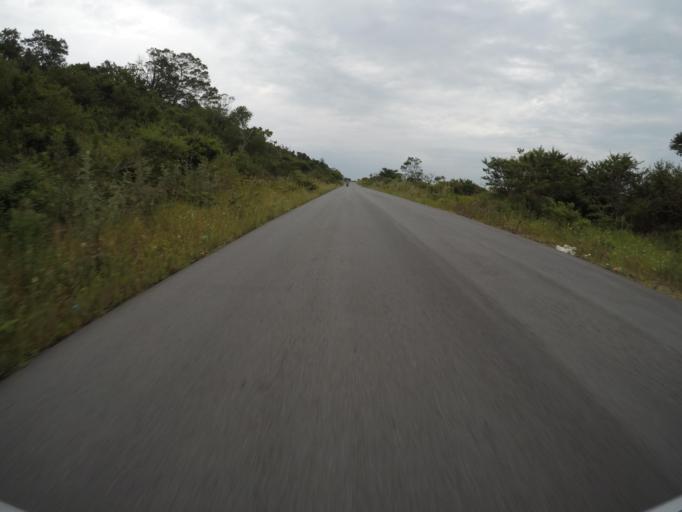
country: ZA
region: Eastern Cape
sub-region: Buffalo City Metropolitan Municipality
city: East London
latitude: -32.9610
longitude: 27.9005
